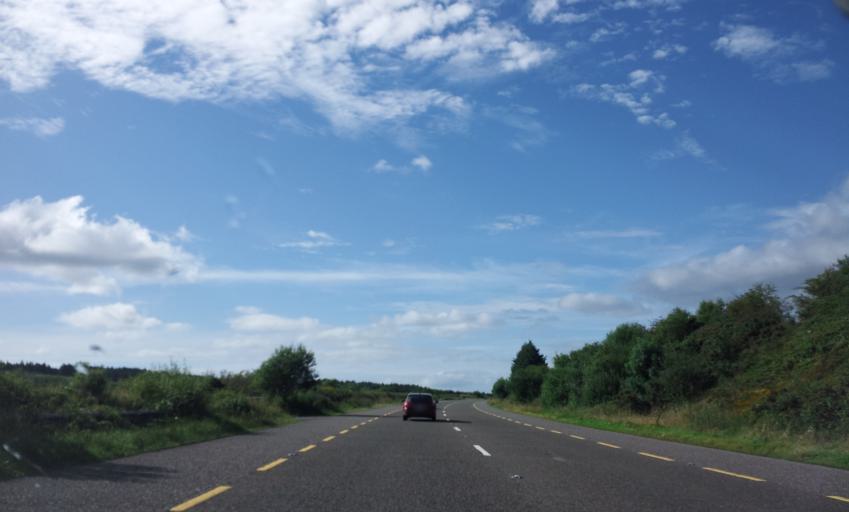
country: IE
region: Munster
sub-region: County Cork
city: Millstreet
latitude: 51.9634
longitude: -9.2451
